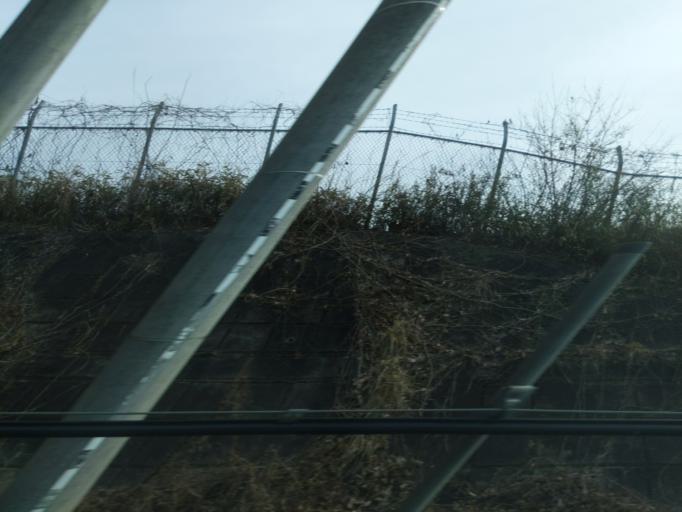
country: JP
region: Iwate
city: Ichinoseki
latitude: 38.8661
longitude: 141.1169
